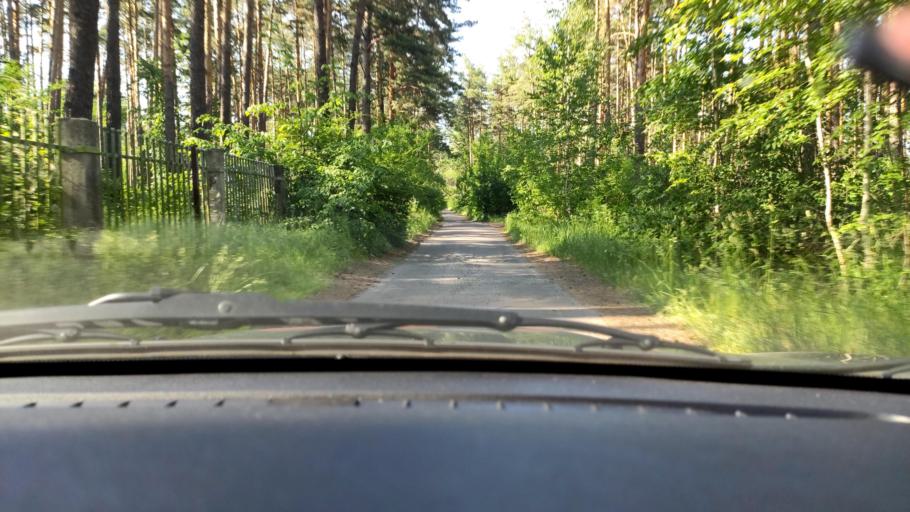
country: RU
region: Voronezj
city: Somovo
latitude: 51.7553
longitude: 39.3745
